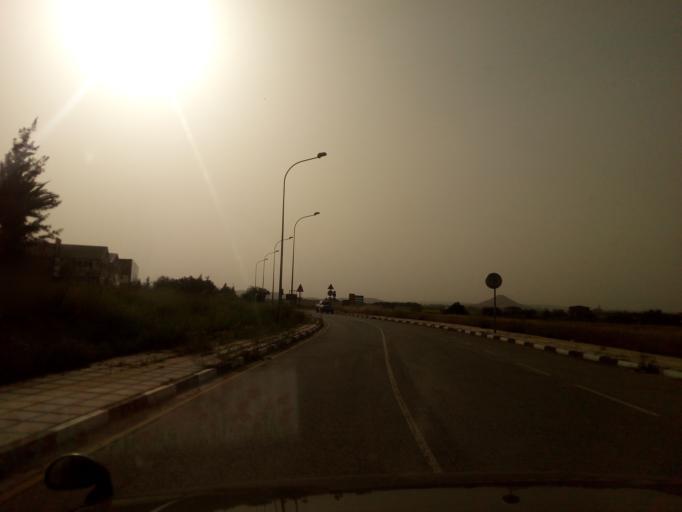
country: CY
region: Larnaka
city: Athienou
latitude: 35.0584
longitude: 33.5221
